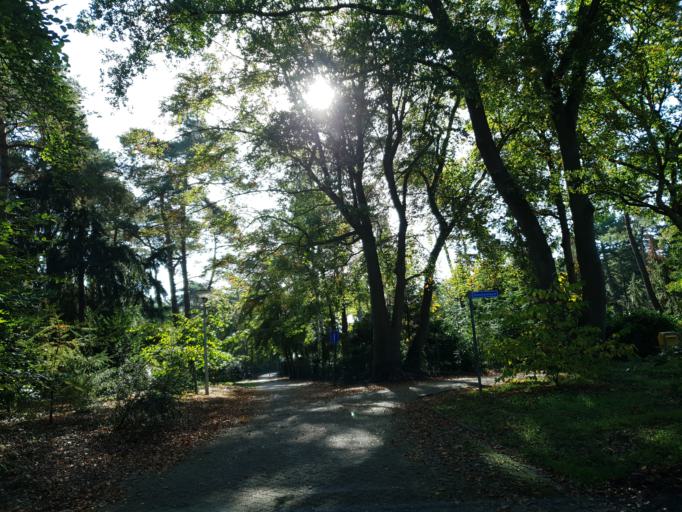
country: NL
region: North Brabant
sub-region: Gemeente Woensdrecht
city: Woensdrecht
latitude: 51.3993
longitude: 4.3357
